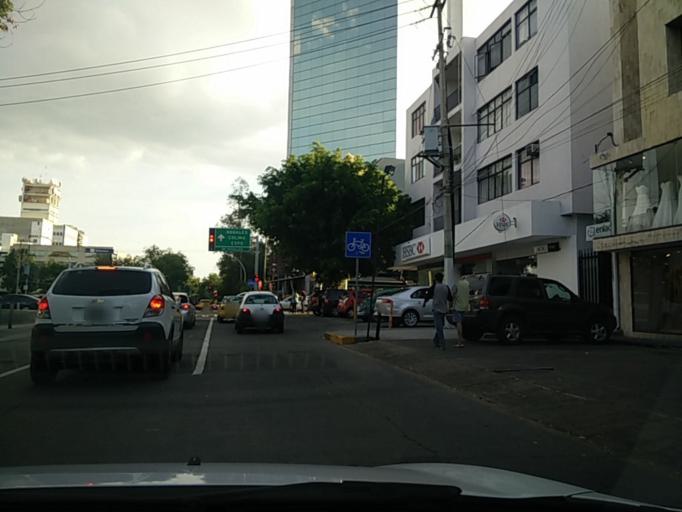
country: MX
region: Jalisco
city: Guadalajara
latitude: 20.6774
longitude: -103.3689
